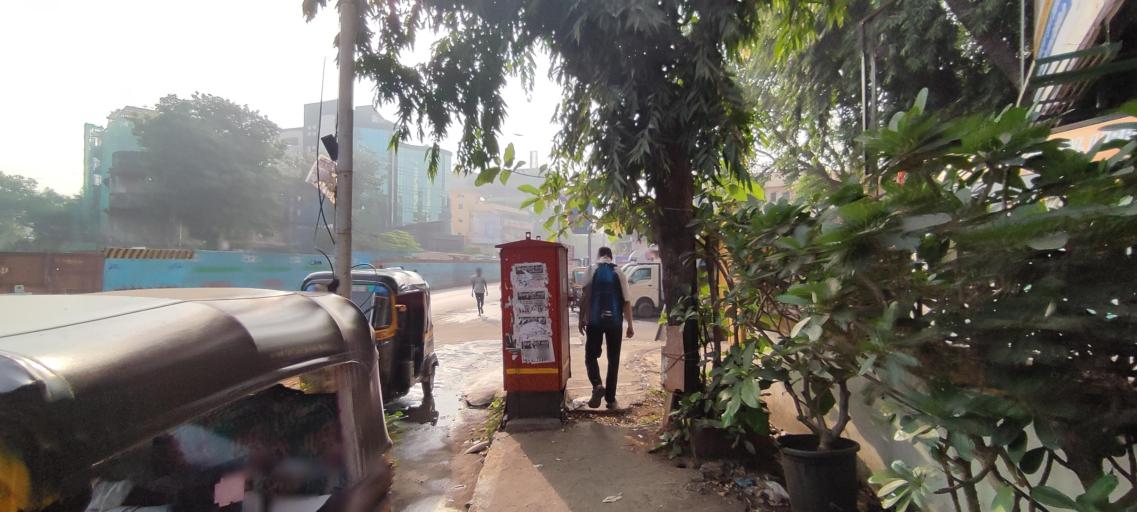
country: IN
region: Maharashtra
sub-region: Mumbai Suburban
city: Mumbai
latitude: 19.0556
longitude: 72.8373
